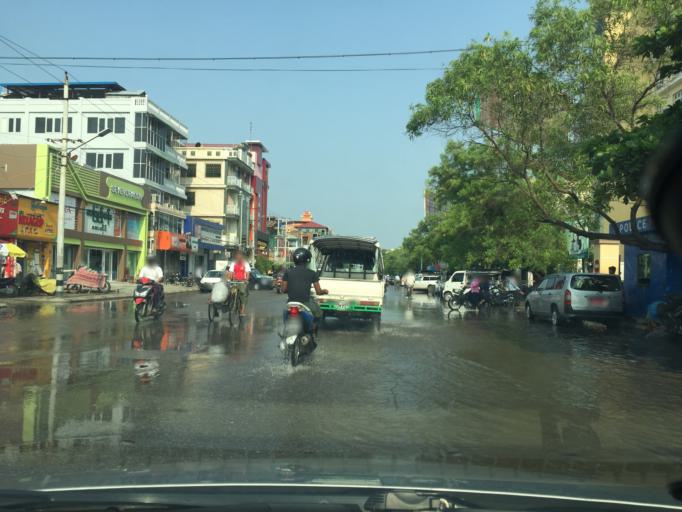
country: MM
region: Mandalay
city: Mandalay
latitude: 21.9766
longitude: 96.0935
